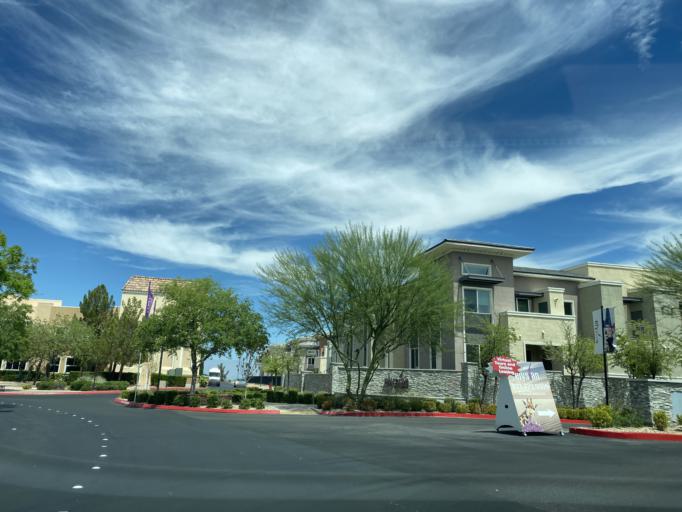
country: US
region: Nevada
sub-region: Clark County
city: Whitney
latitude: 36.0225
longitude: -115.0819
